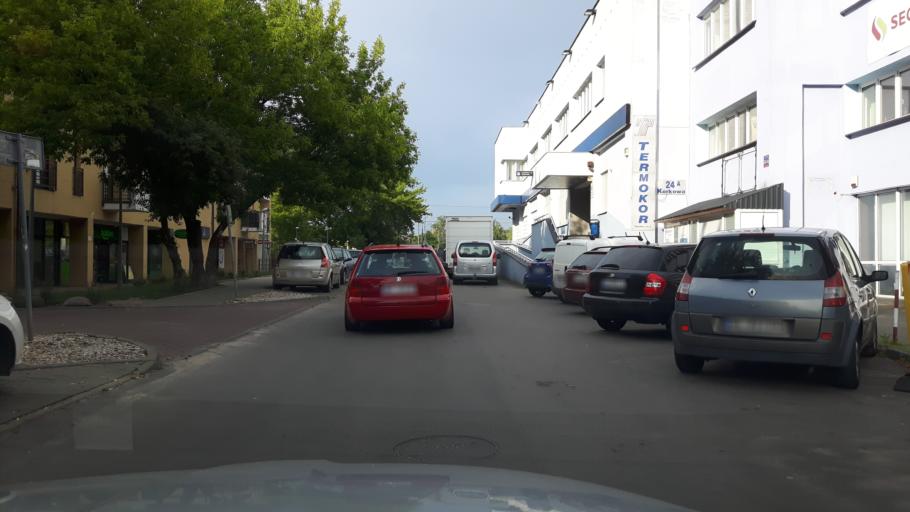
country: PL
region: Masovian Voivodeship
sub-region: Warszawa
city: Rembertow
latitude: 52.2355
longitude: 21.1355
